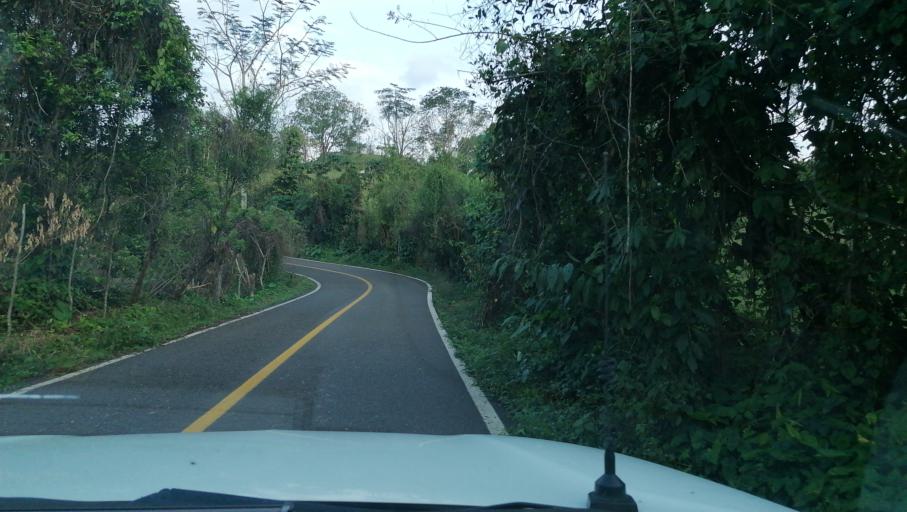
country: MX
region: Chiapas
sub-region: Juarez
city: El Triunfo 1ra. Seccion (Cardona)
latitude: 17.5008
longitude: -93.2417
